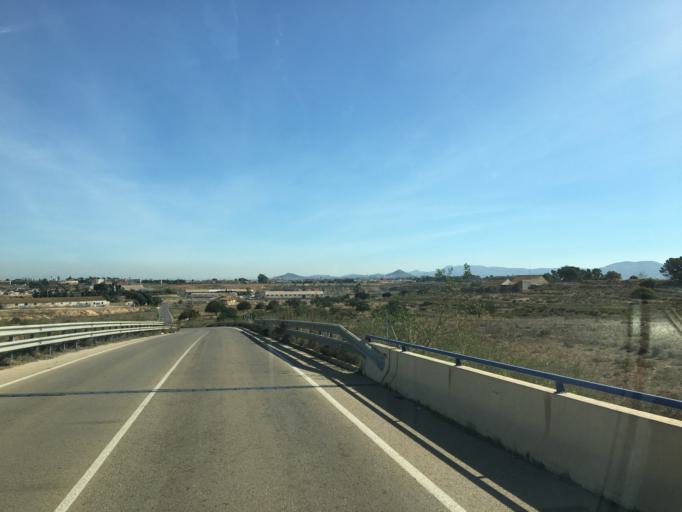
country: ES
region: Murcia
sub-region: Murcia
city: Cartagena
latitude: 37.6317
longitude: -1.0289
